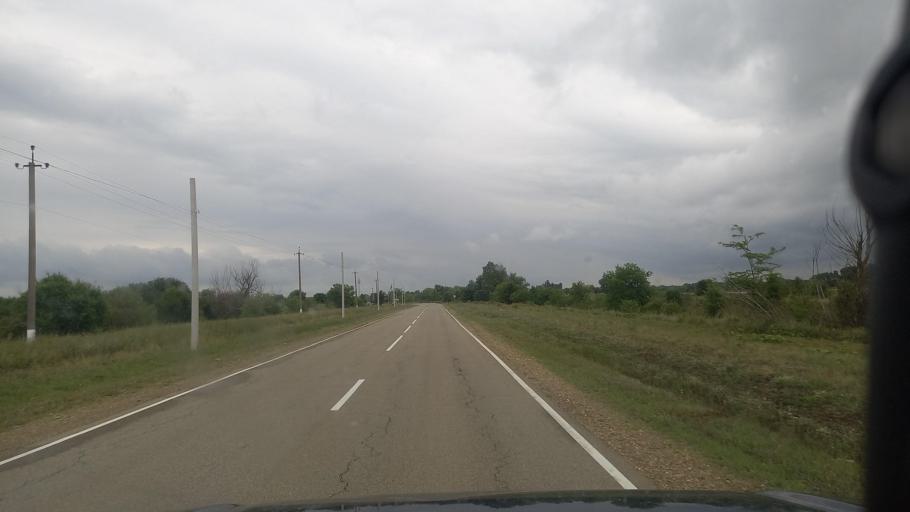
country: RU
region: Adygeya
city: Adygeysk
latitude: 44.8849
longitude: 39.2492
